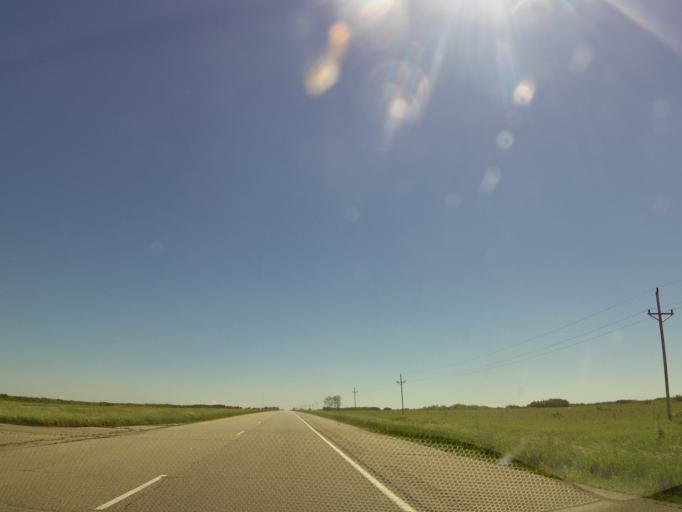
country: US
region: Minnesota
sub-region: Red Lake County
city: Red Lake Falls
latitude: 47.7603
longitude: -96.3902
